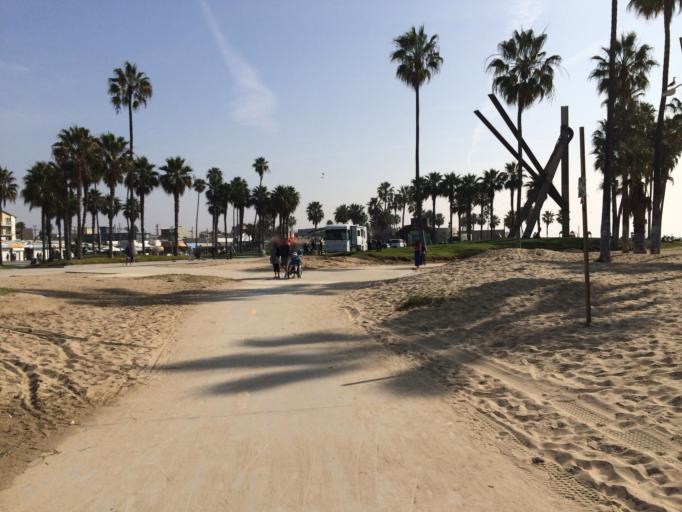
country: US
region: California
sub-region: Los Angeles County
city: Marina del Rey
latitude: 33.9870
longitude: -118.4749
